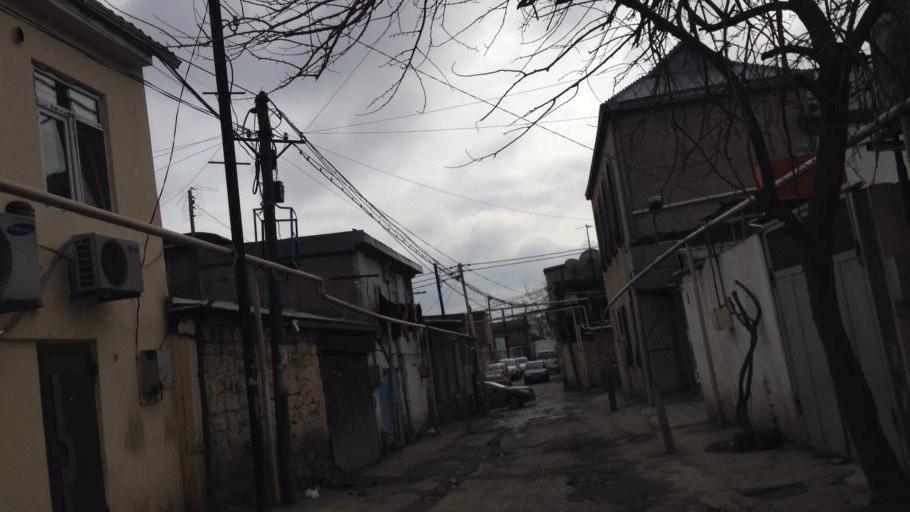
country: AZ
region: Baki
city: Bilajari
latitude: 40.4010
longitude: 49.8276
